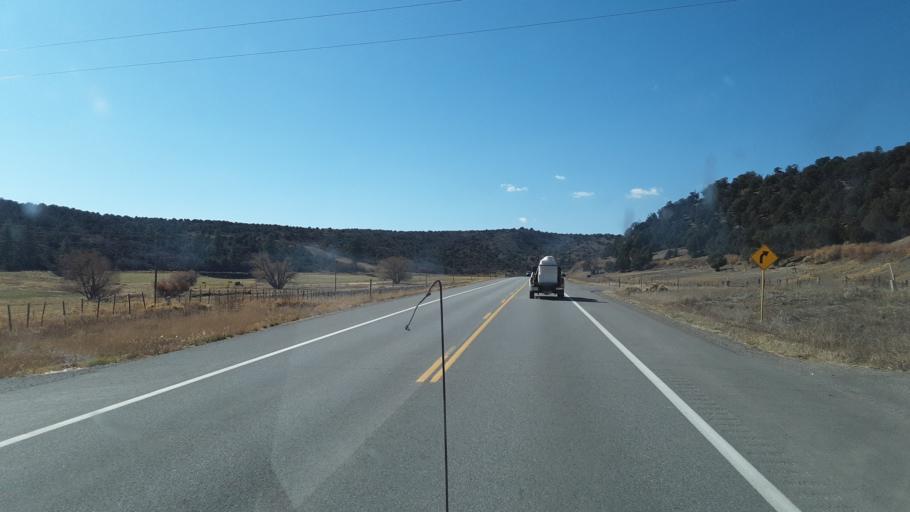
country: US
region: Colorado
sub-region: La Plata County
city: Bayfield
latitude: 37.2243
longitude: -107.6728
